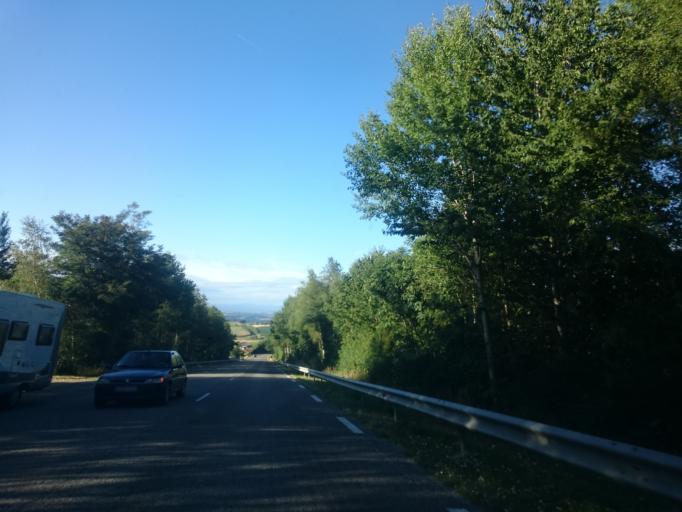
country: FR
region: Midi-Pyrenees
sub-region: Departement de l'Aveyron
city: Entraygues-sur-Truyere
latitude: 44.7194
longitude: 2.5036
